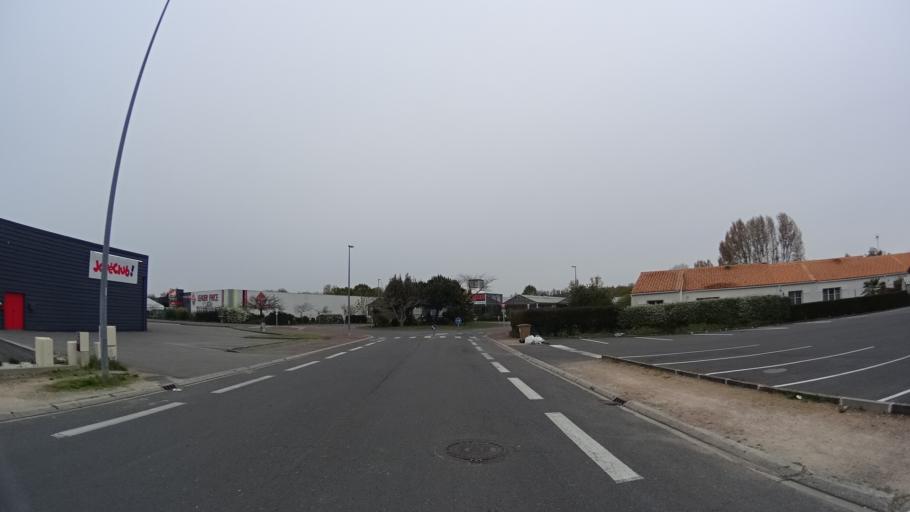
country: FR
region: Pays de la Loire
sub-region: Departement de la Vendee
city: Challans
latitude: 46.8524
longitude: -1.8887
